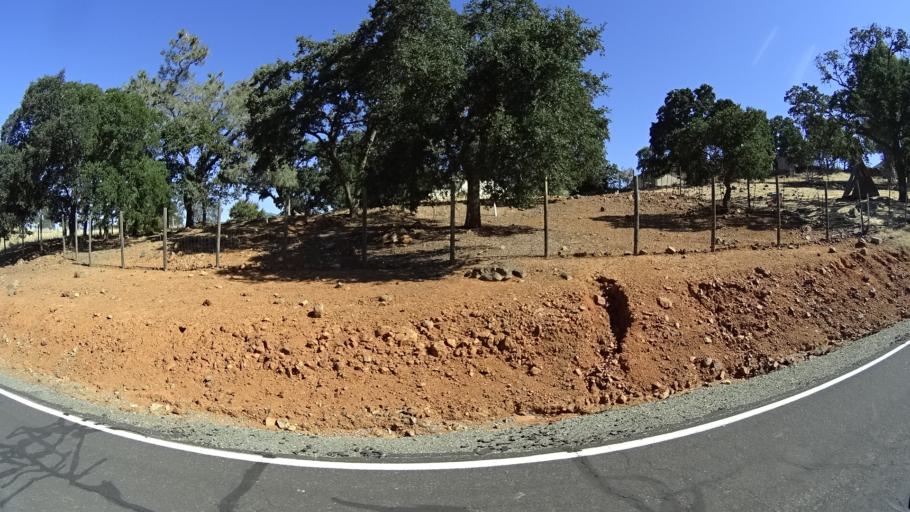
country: US
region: California
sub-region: Calaveras County
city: Rancho Calaveras
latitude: 38.0944
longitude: -120.8581
